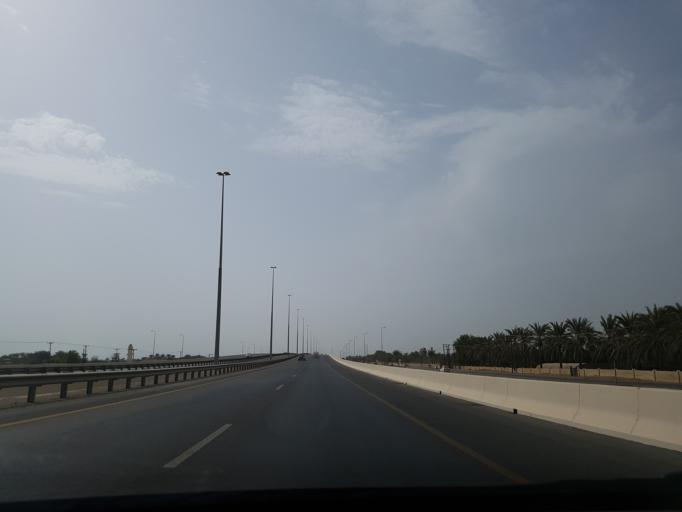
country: OM
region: Al Batinah
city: Saham
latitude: 24.1079
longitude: 56.9155
